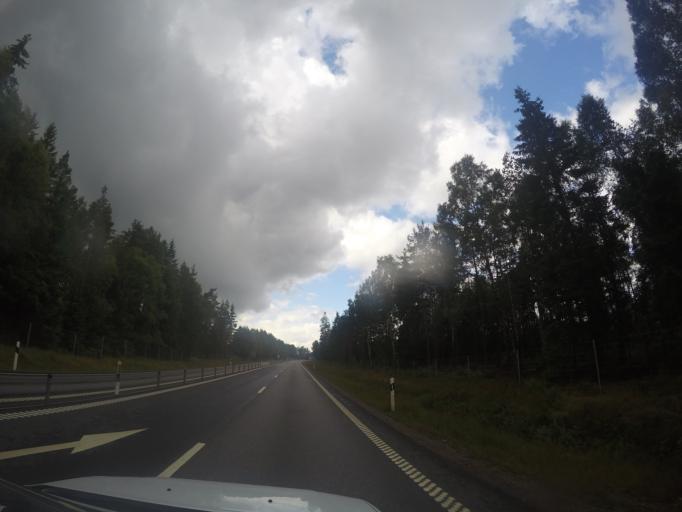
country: SE
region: Kronoberg
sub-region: Ljungby Kommun
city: Ljungby
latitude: 56.8062
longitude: 13.8829
